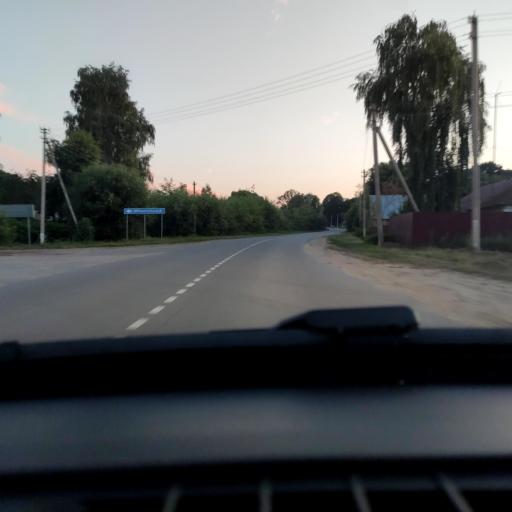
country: RU
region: Lipetsk
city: Zadonsk
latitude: 52.2876
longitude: 38.7516
